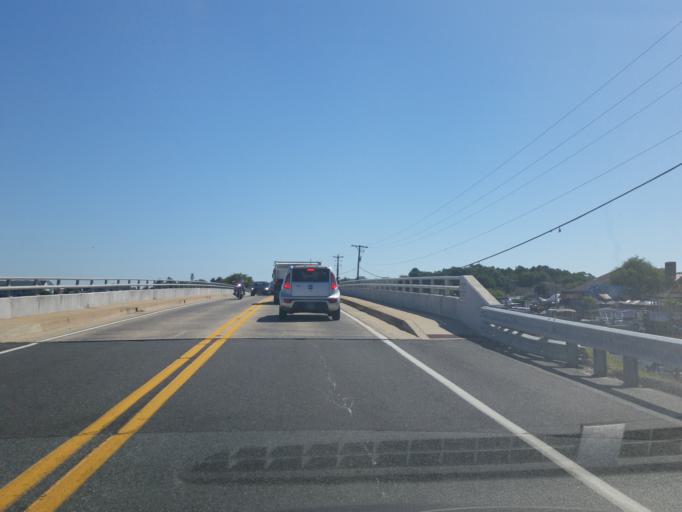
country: US
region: Delaware
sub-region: Sussex County
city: Bethany Beach
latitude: 38.4527
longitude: -75.0650
